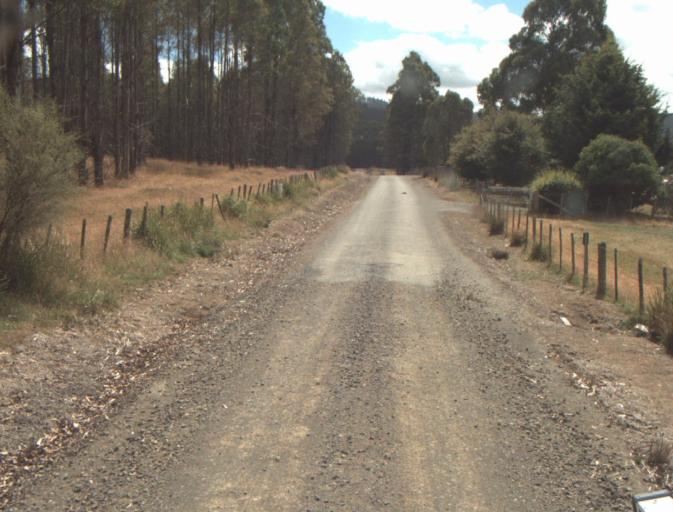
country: AU
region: Tasmania
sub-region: Dorset
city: Scottsdale
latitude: -41.4161
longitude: 147.5244
